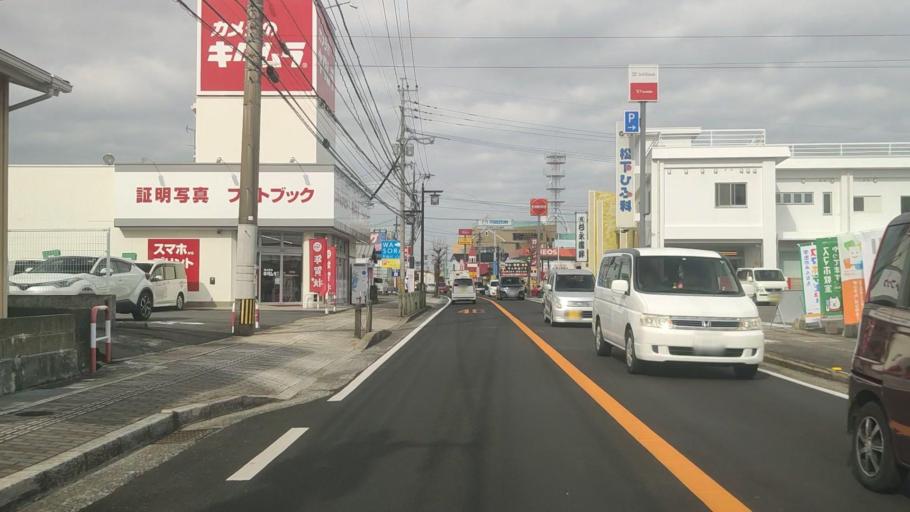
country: JP
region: Nagasaki
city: Shimabara
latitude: 32.7956
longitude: 130.3678
